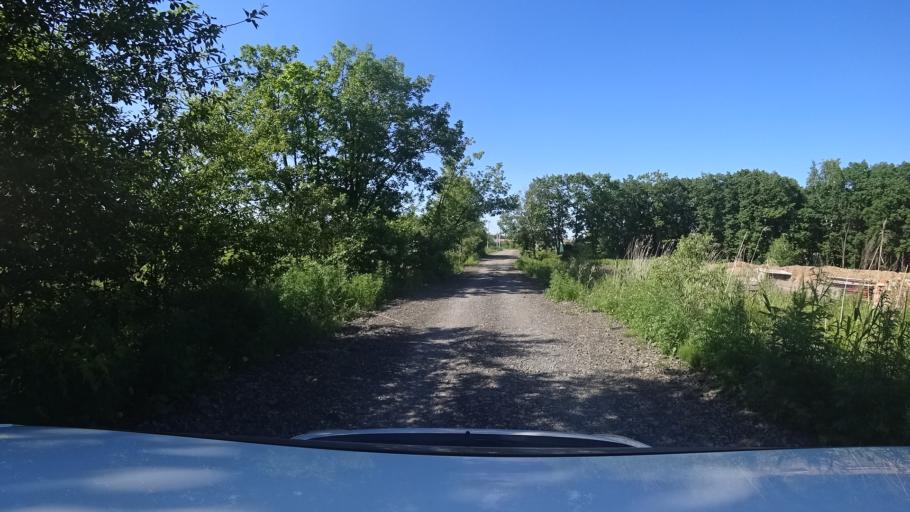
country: RU
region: Khabarovsk Krai
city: Topolevo
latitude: 48.5481
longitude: 135.1825
